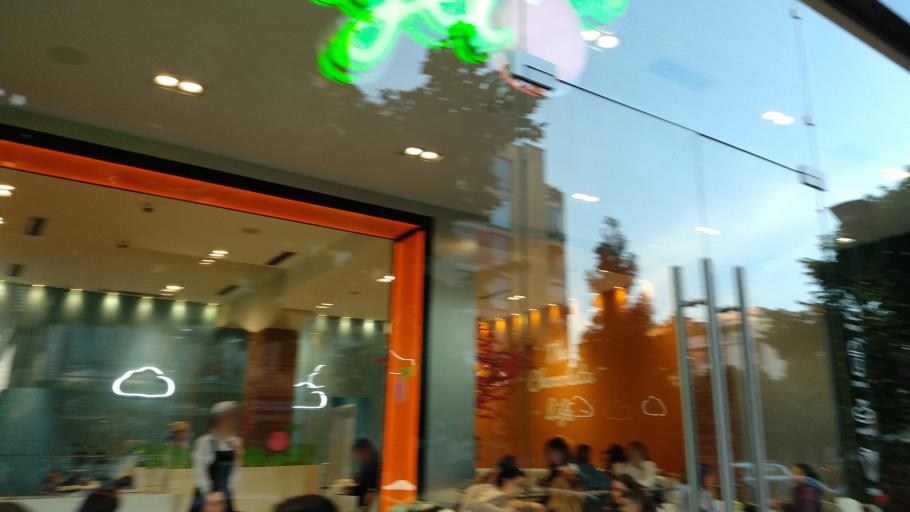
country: AL
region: Tirane
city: Tirana
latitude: 41.3277
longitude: 19.8028
